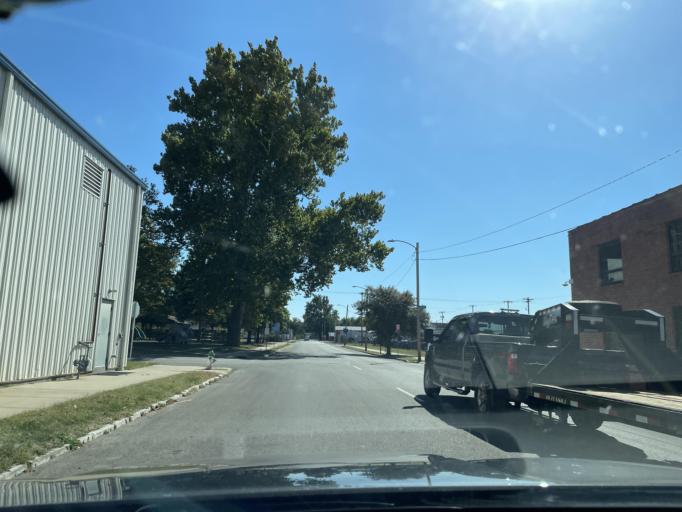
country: US
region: Missouri
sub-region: Buchanan County
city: Saint Joseph
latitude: 39.7575
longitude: -94.8493
